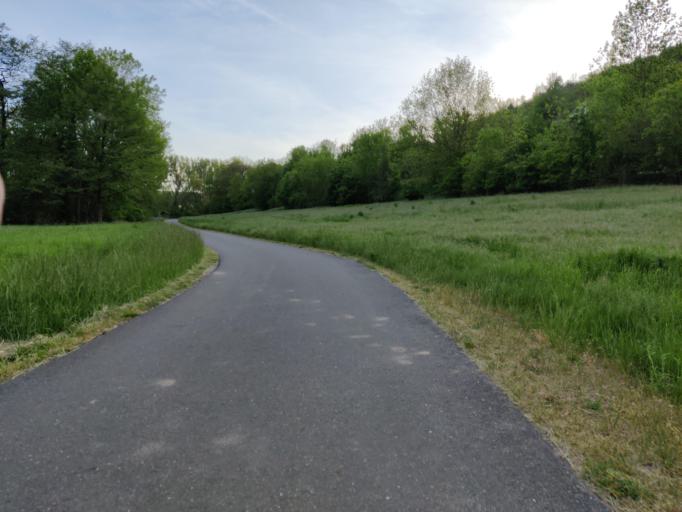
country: DE
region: Saxony-Anhalt
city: Balgstadt
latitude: 51.2108
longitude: 11.7365
